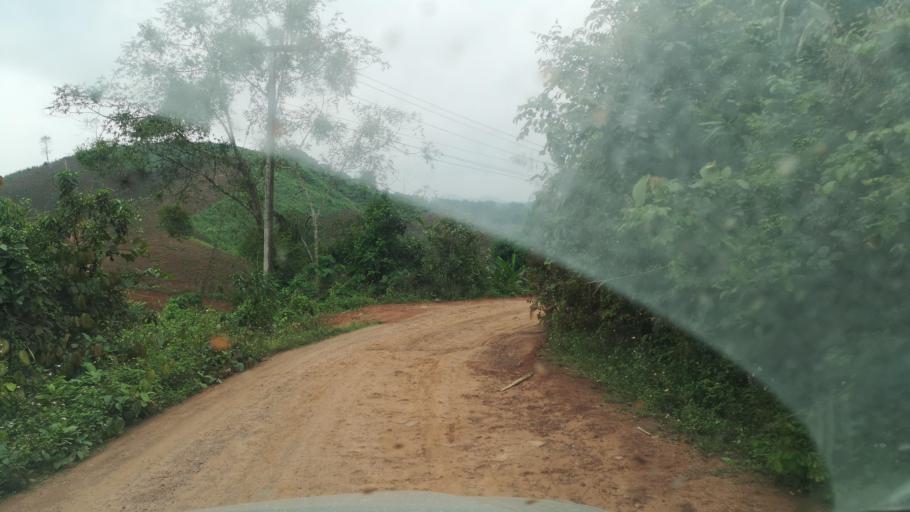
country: LA
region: Oudomxai
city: Muang La
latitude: 21.0717
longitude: 101.8415
